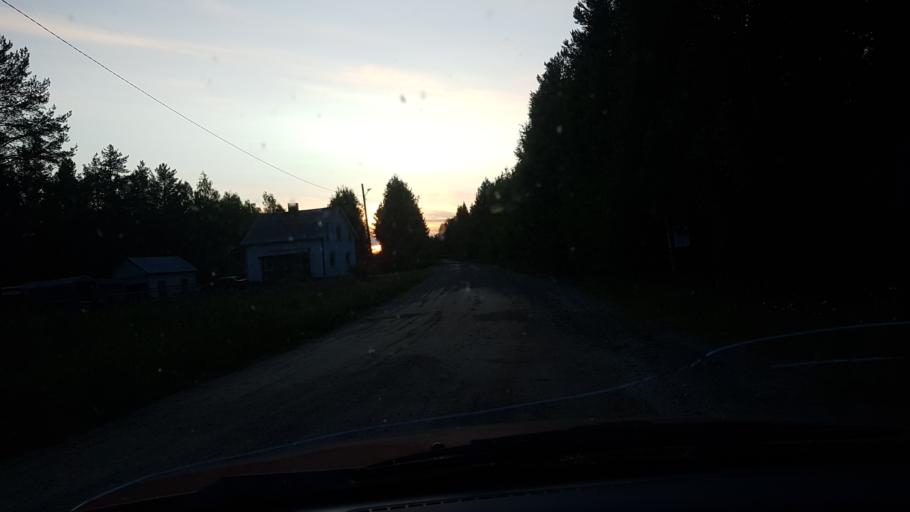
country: SE
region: Norrbotten
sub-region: Alvsbyns Kommun
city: AElvsbyn
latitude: 65.6938
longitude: 20.6729
